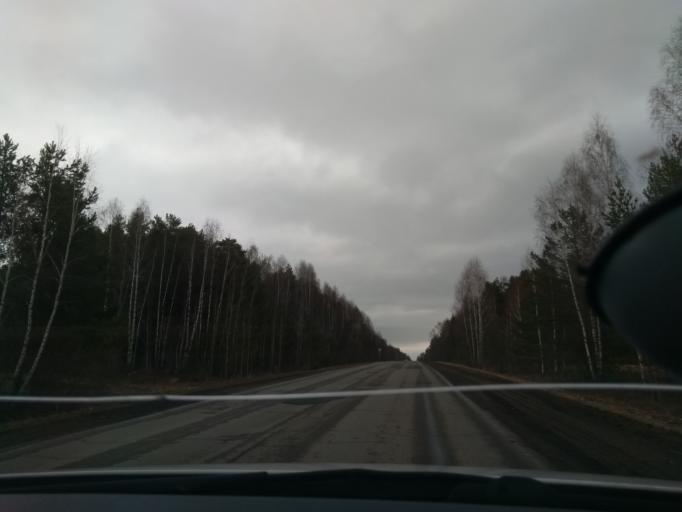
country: RU
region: Perm
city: Kungur
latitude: 57.3585
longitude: 56.8128
